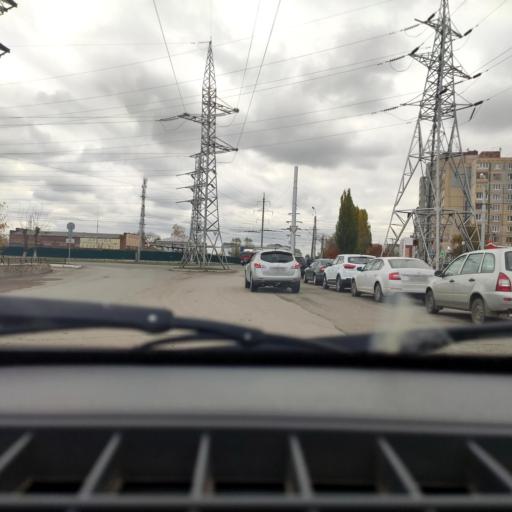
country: RU
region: Bashkortostan
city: Ufa
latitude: 54.7976
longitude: 56.0568
